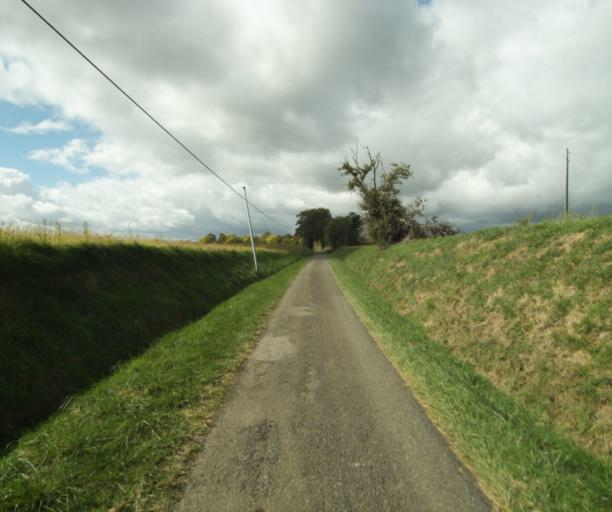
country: FR
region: Midi-Pyrenees
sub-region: Departement du Gers
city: Cazaubon
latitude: 43.8544
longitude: -0.0233
